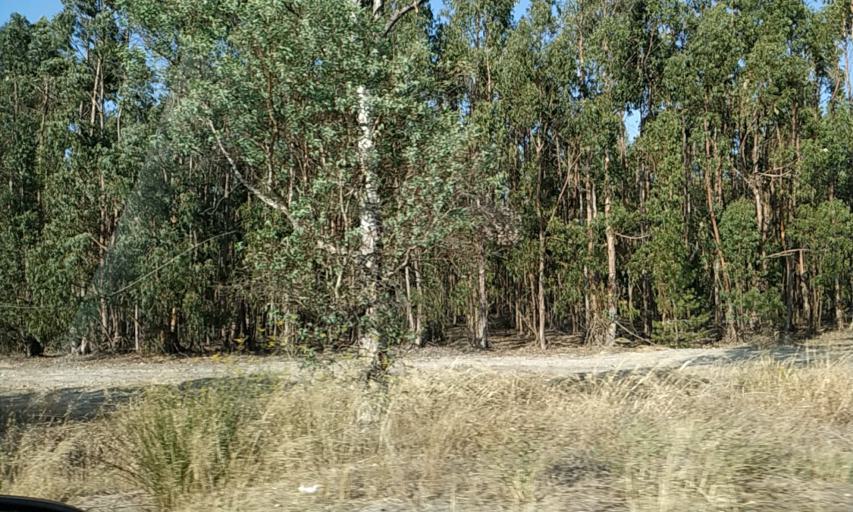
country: PT
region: Santarem
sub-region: Almeirim
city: Fazendas de Almeirim
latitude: 39.1445
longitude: -8.6146
